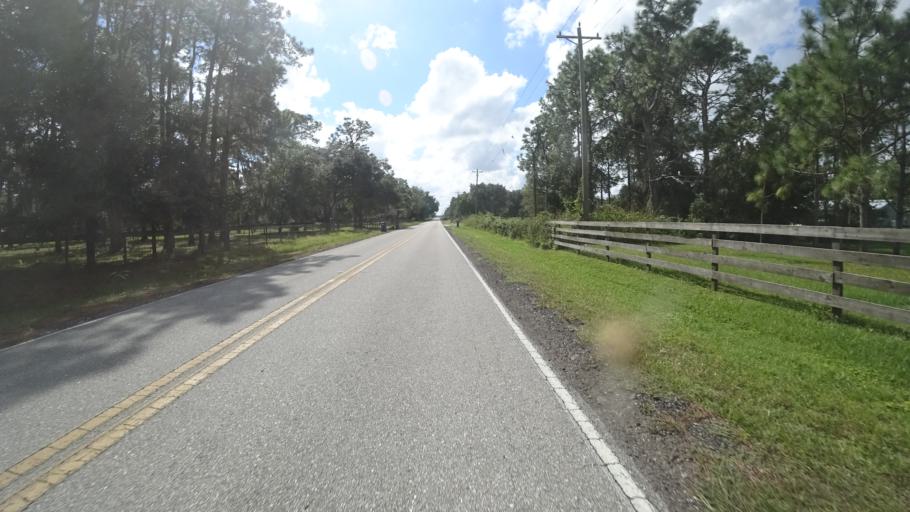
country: US
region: Florida
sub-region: Hillsborough County
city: Wimauma
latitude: 27.4295
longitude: -82.1331
